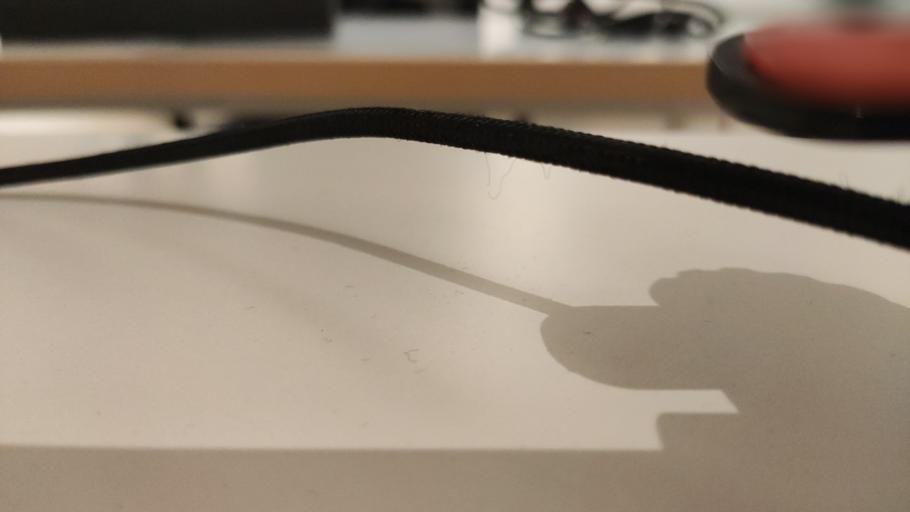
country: RU
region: Moskovskaya
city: Dorokhovo
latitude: 55.5147
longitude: 36.3501
